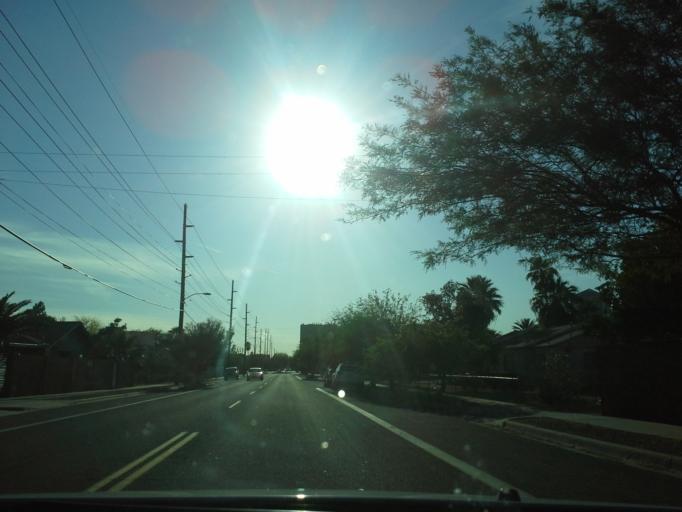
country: US
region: Arizona
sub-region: Maricopa County
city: Phoenix
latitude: 33.4766
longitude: -112.0610
